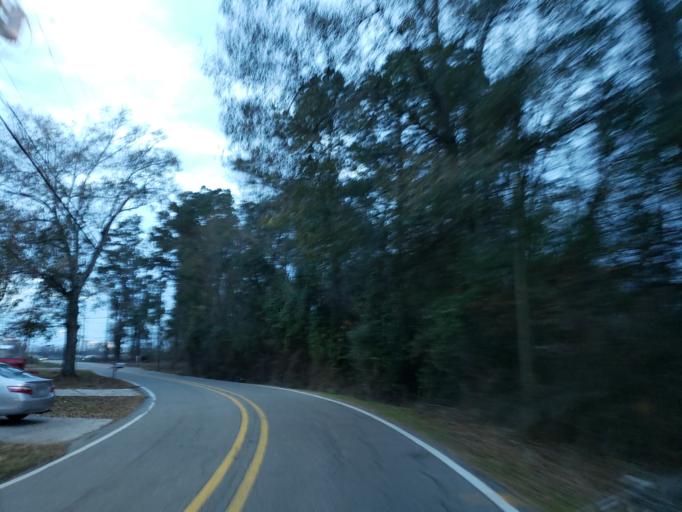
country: US
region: Mississippi
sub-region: Forrest County
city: Petal
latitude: 31.3342
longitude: -89.2601
